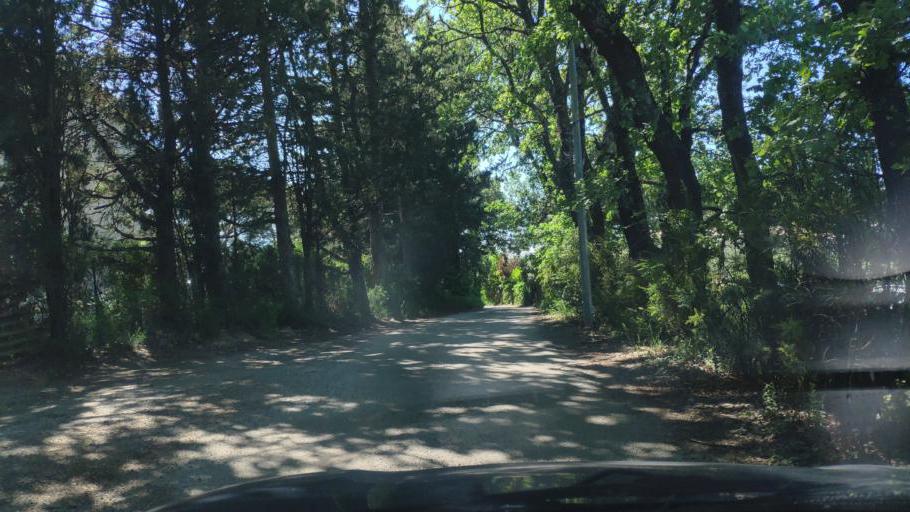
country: FR
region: Provence-Alpes-Cote d'Azur
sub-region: Departement du Vaucluse
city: Carpentras
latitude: 44.0803
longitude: 5.0518
